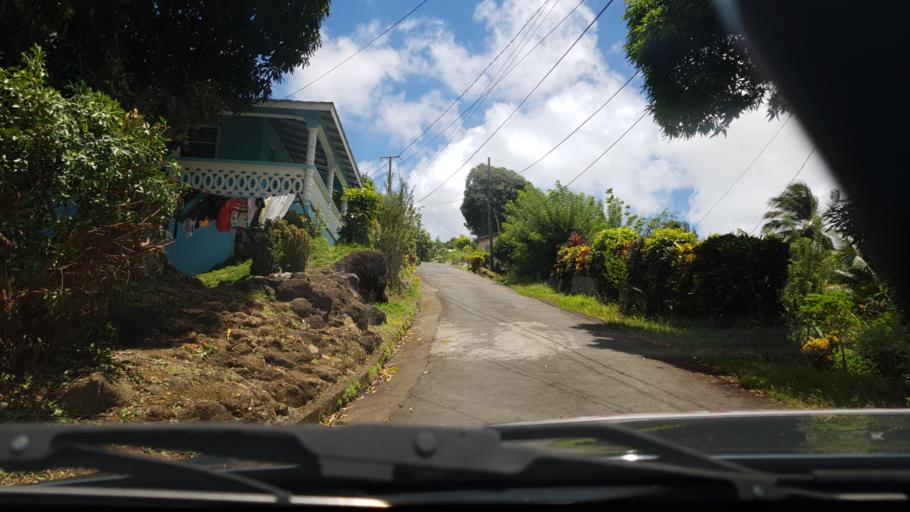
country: LC
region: Anse-la-Raye
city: Anse La Raye
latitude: 13.9534
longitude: -61.0006
